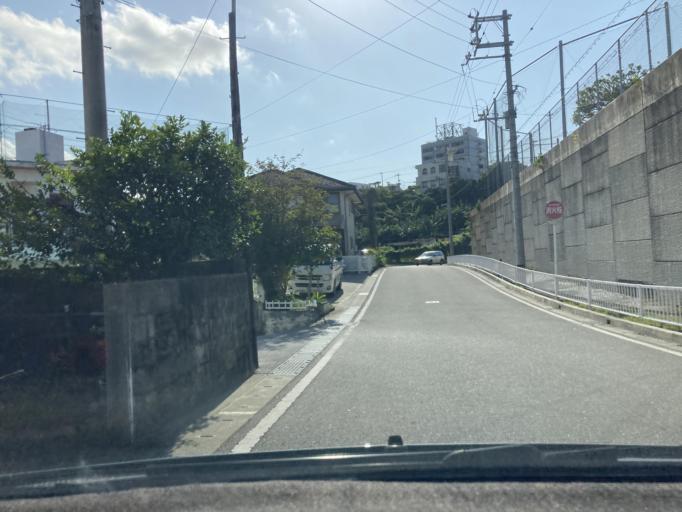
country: JP
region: Okinawa
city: Tomigusuku
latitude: 26.1803
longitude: 127.6826
